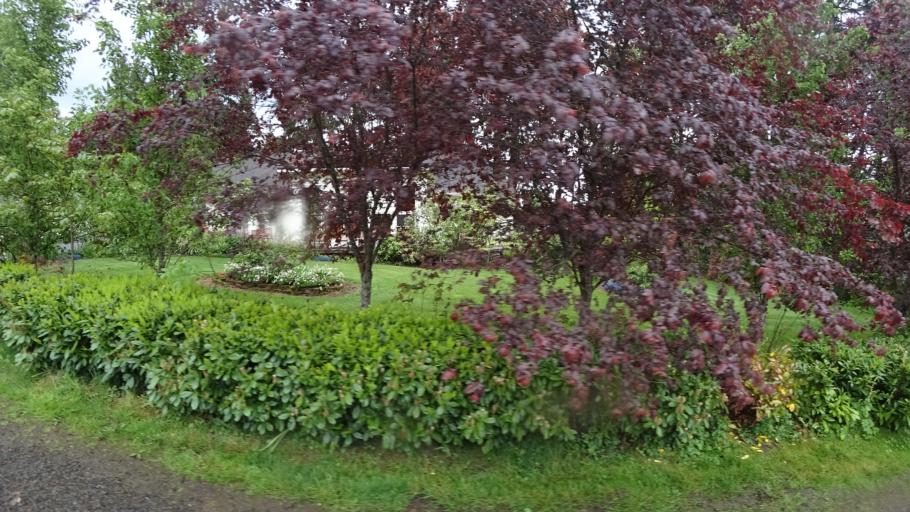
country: US
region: Oregon
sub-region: Washington County
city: West Haven
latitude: 45.5303
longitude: -122.7671
